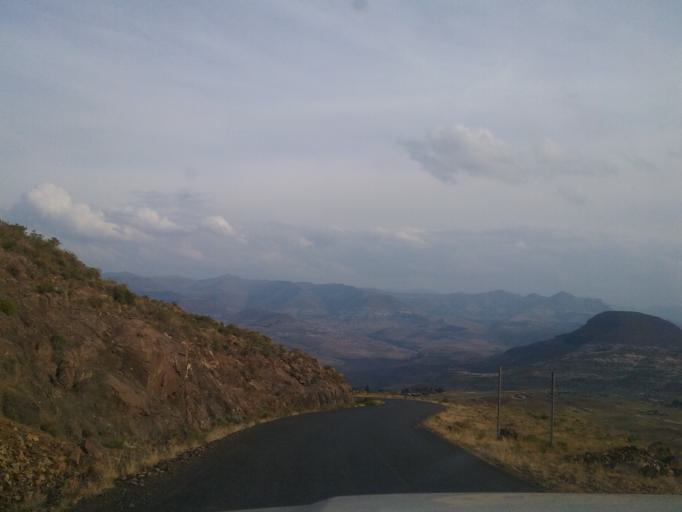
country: LS
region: Quthing
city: Quthing
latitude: -30.1947
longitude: 27.9708
